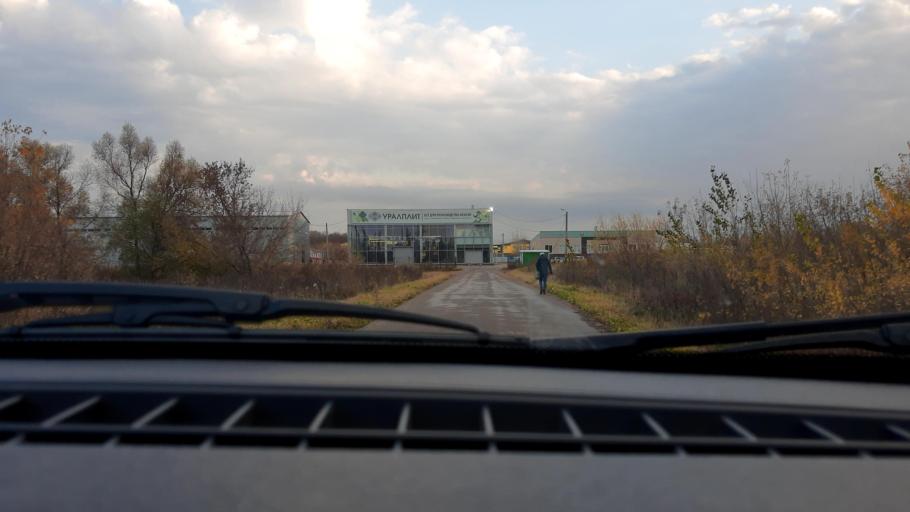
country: RU
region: Bashkortostan
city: Ufa
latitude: 54.7650
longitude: 55.9583
